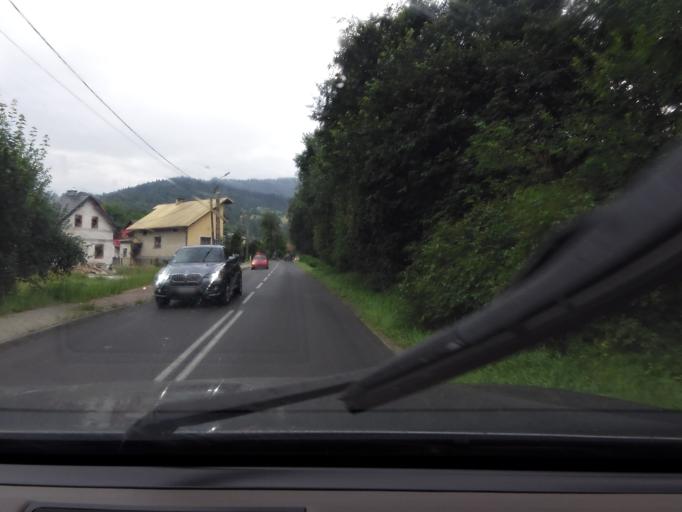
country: PL
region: Silesian Voivodeship
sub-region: Powiat zywiecki
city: Milowka
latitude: 49.5466
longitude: 19.0998
